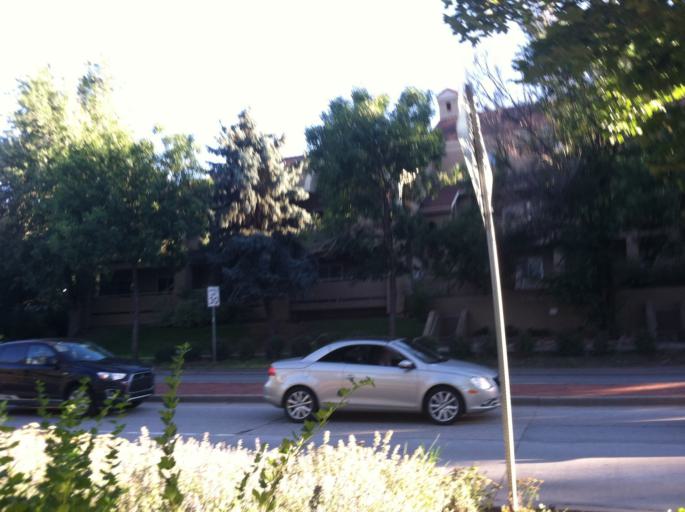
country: US
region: Colorado
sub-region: Boulder County
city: Boulder
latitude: 40.0043
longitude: -105.2691
